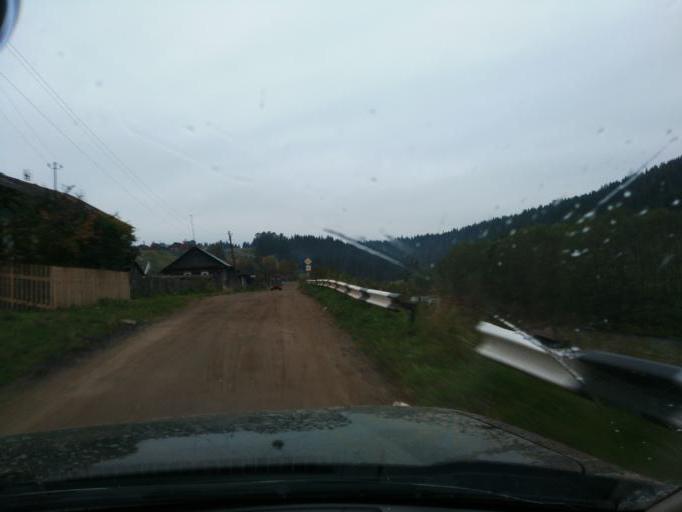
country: RU
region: Sverdlovsk
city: Sylva
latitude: 57.8600
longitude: 58.6301
